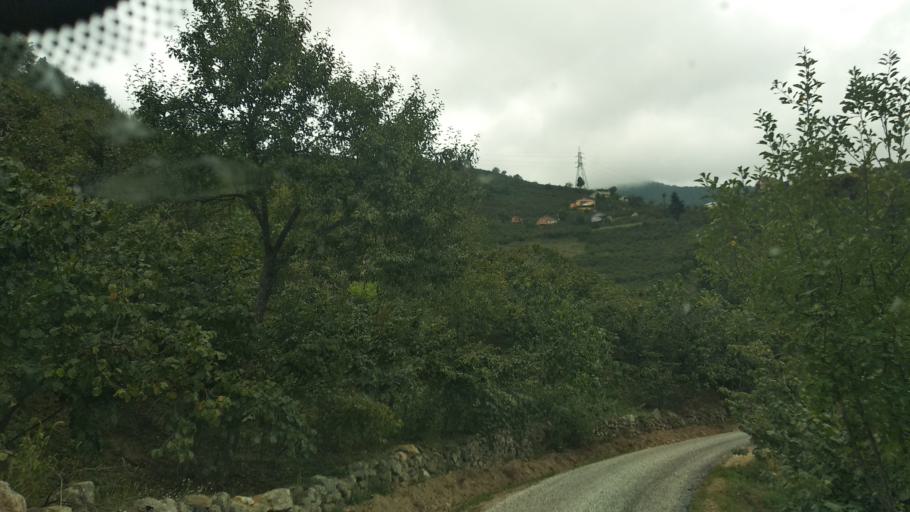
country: TR
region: Giresun
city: Dogankent
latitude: 40.7411
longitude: 38.9924
